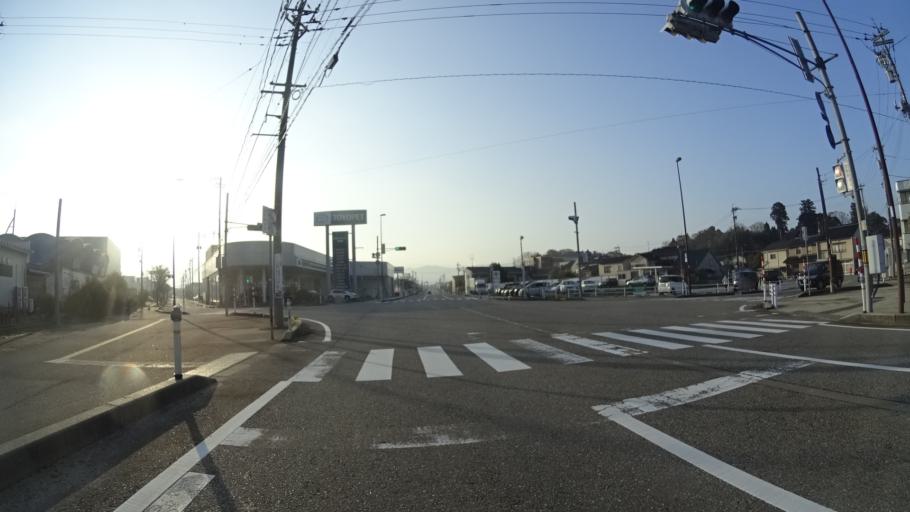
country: JP
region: Ishikawa
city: Nanao
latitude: 37.0531
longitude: 136.9556
